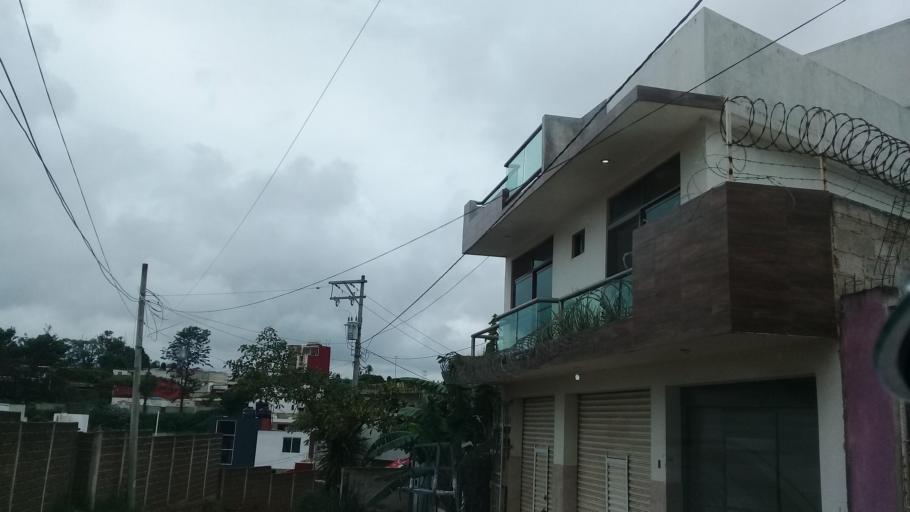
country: MX
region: Veracruz
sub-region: Emiliano Zapata
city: Las Trancas
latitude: 19.4983
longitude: -96.8686
